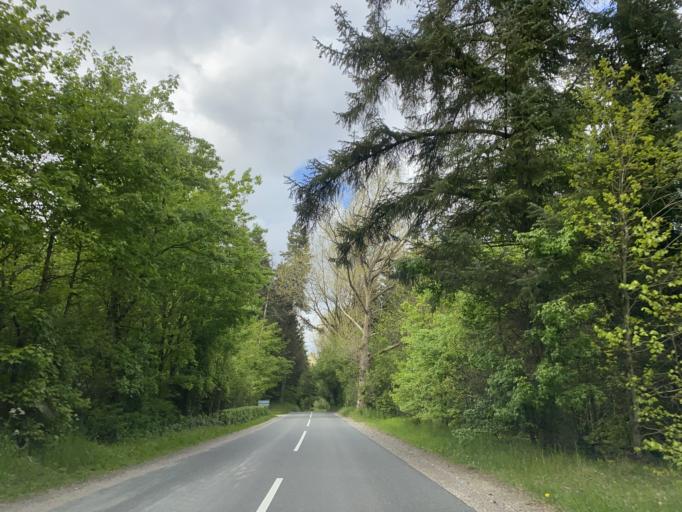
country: DK
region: Central Jutland
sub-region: Horsens Kommune
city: Braedstrup
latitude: 56.0310
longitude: 9.6557
